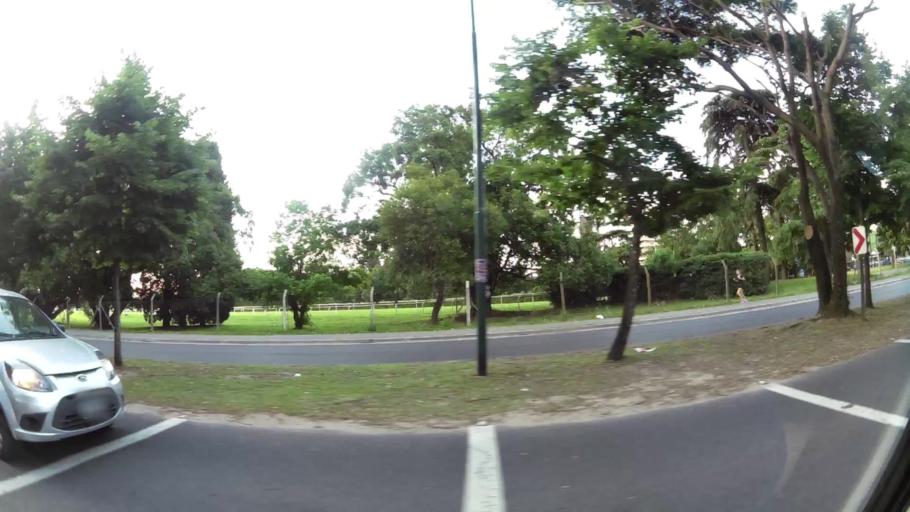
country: AR
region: Buenos Aires
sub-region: Partido de San Isidro
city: San Isidro
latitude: -34.4806
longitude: -58.5079
